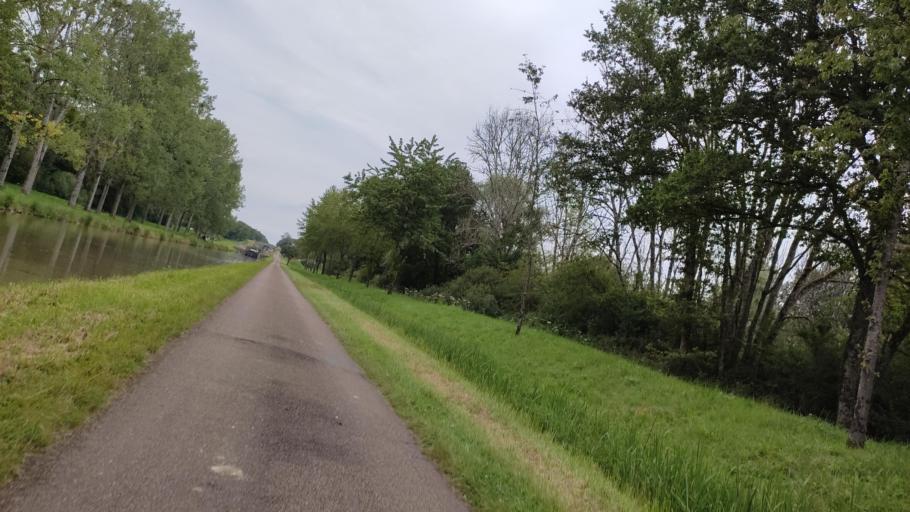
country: FR
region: Bourgogne
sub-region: Departement de la Nievre
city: Chatillon-en-Bazois
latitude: 47.1050
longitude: 3.6342
